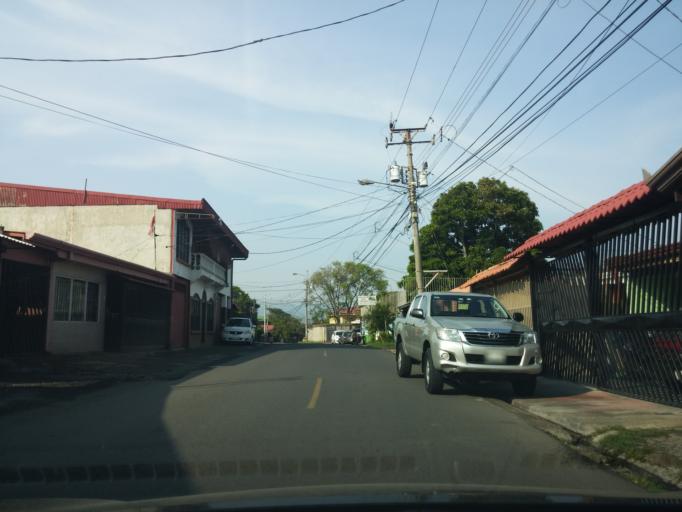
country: CR
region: Heredia
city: Llorente
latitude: 9.9981
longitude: -84.1434
